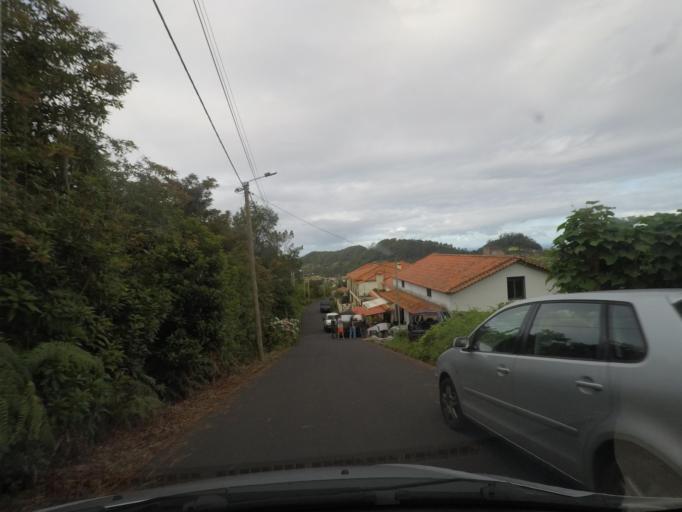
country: PT
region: Madeira
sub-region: Santana
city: Santana
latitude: 32.7928
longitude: -16.8776
